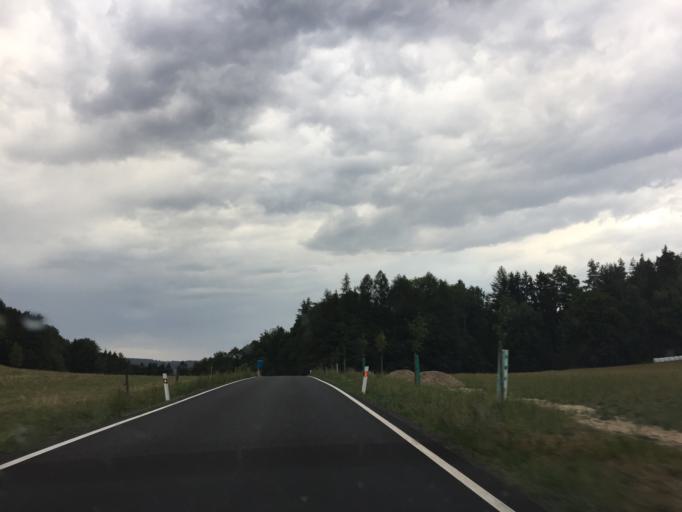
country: CZ
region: Liberecky
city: Mala Skala
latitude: 50.6311
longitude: 15.2152
